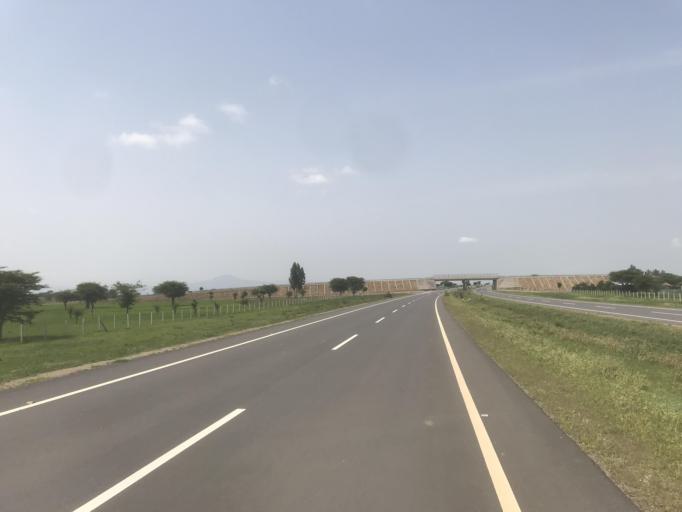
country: ET
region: Oromiya
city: Mojo
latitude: 8.4798
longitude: 39.0500
